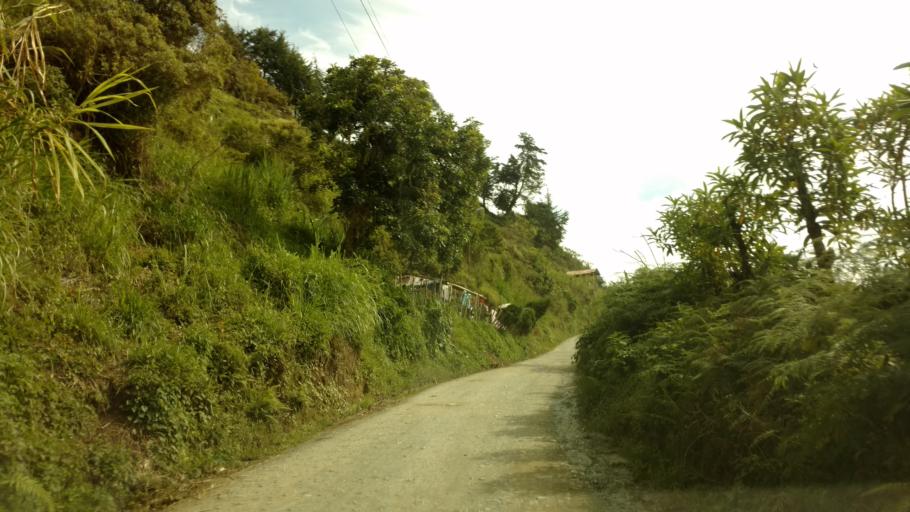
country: CO
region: Caldas
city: Aguadas
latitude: 5.6208
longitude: -75.4536
